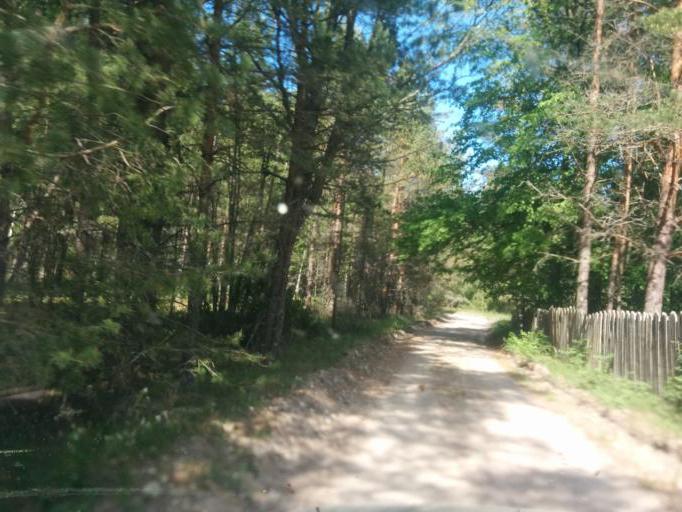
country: LV
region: Dundaga
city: Dundaga
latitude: 57.6247
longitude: 22.1061
